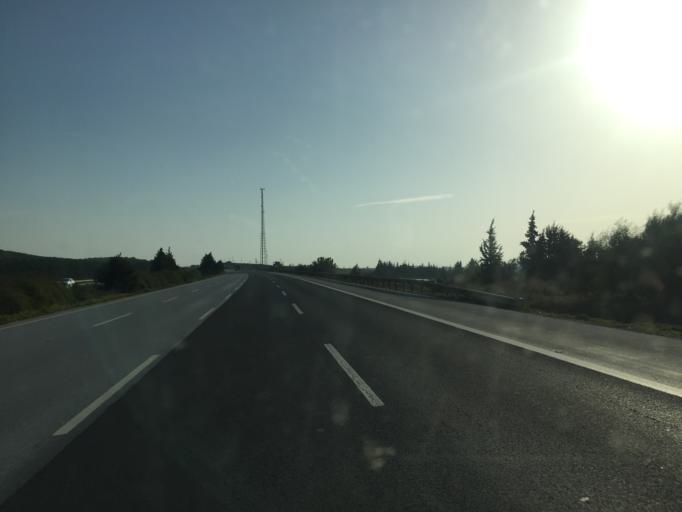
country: TR
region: Mersin
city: Yenice
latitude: 37.0227
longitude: 35.0798
